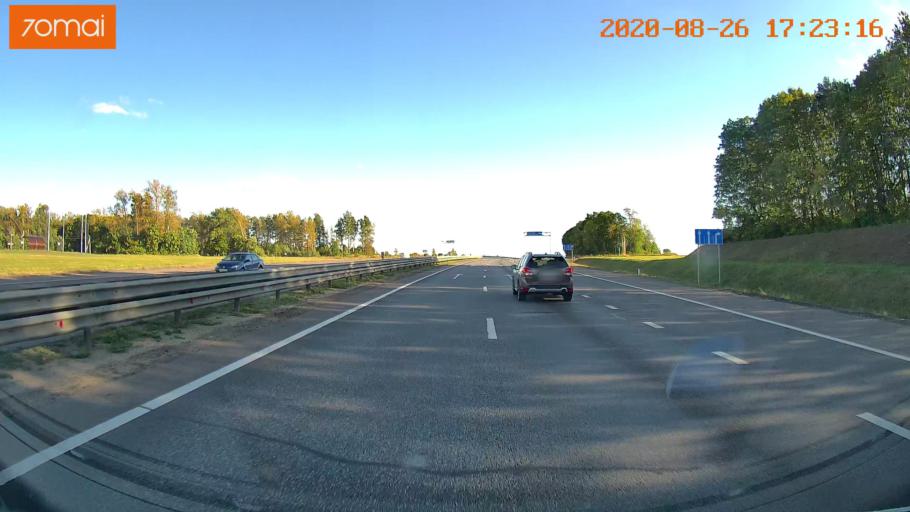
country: RU
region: Tula
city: Volovo
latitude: 53.5372
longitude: 38.1185
